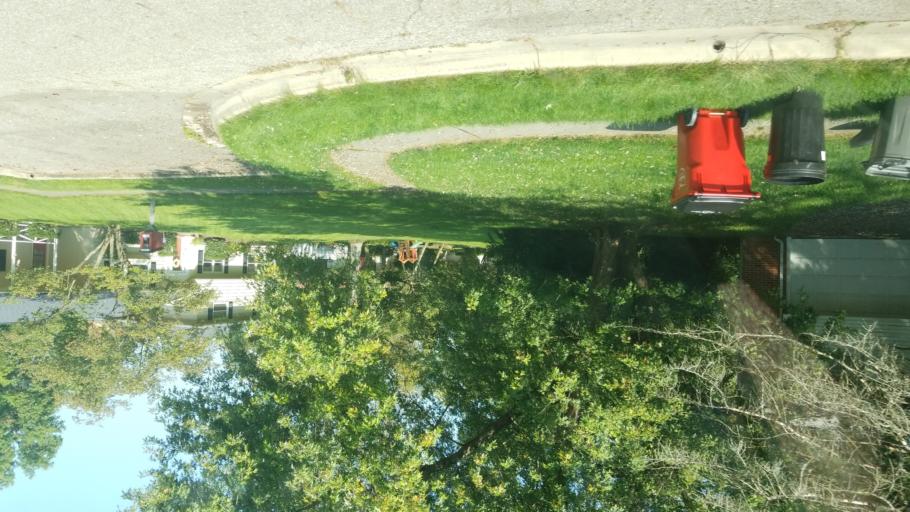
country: US
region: Ohio
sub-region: Franklin County
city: Worthington
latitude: 40.0778
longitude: -83.0248
